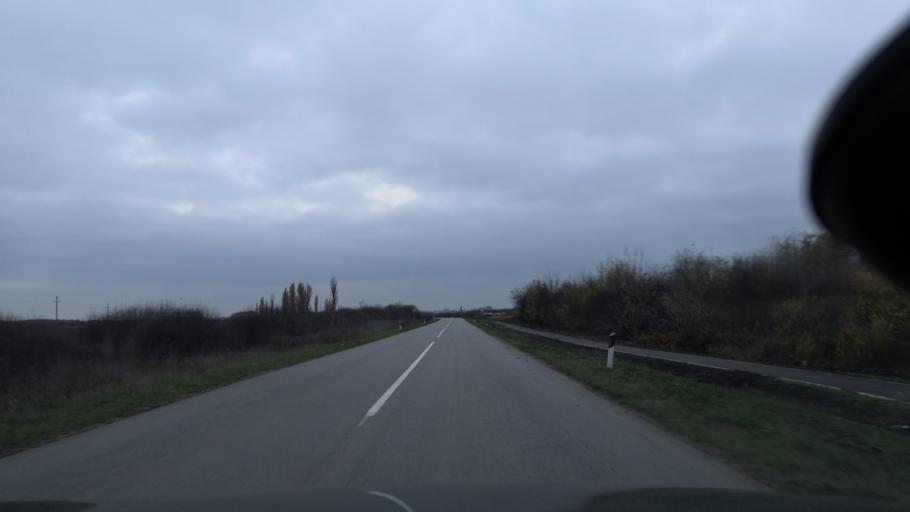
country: RS
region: Autonomna Pokrajina Vojvodina
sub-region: Severnobanatski Okrug
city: Novi Knezevac
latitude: 46.0786
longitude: 20.1043
